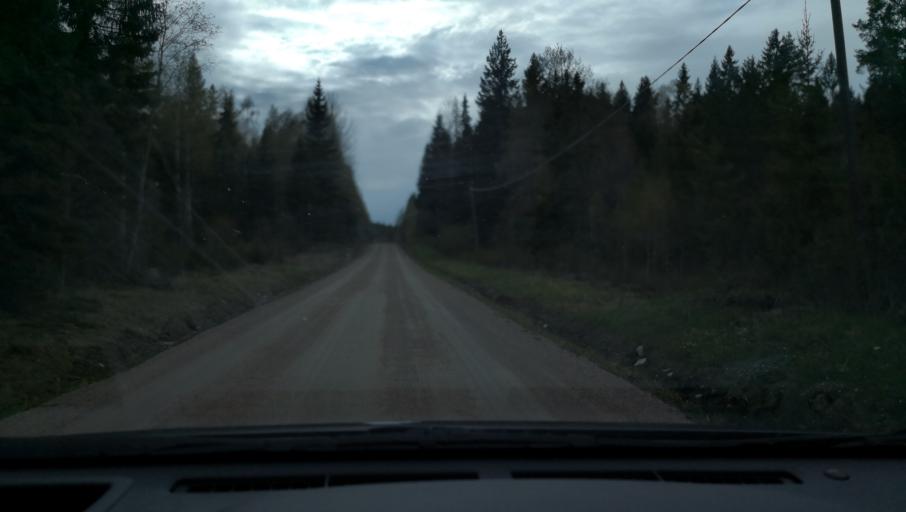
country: SE
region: Vaestmanland
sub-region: Fagersta Kommun
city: Fagersta
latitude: 60.1215
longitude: 15.7297
